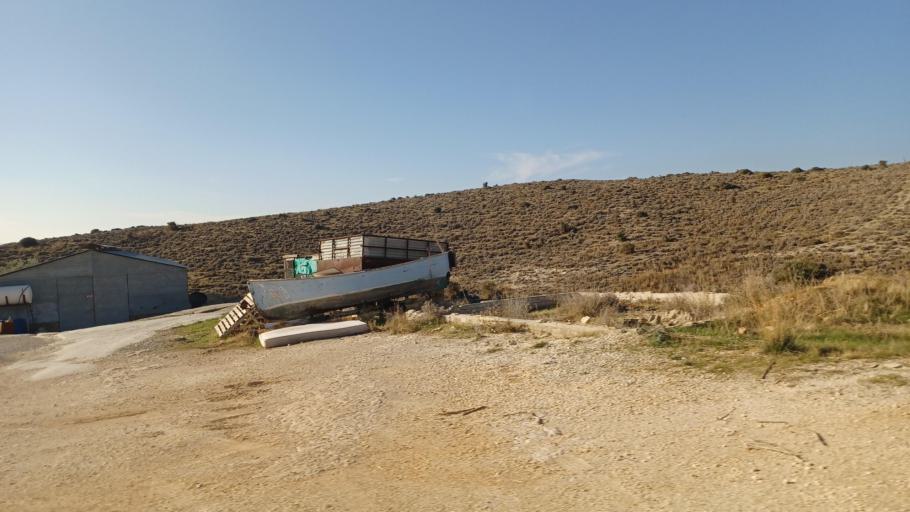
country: CY
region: Larnaka
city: Psevdas
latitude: 34.9396
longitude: 33.5228
